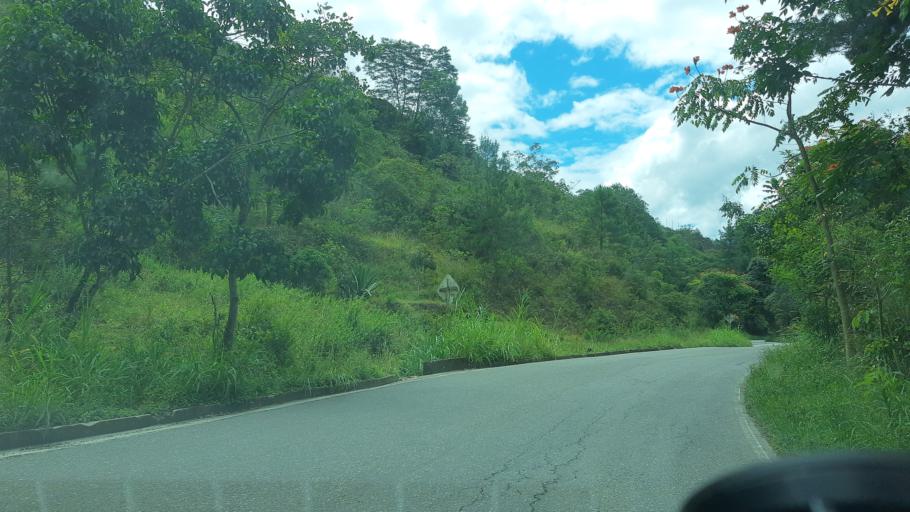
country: CO
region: Boyaca
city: Garagoa
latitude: 5.0483
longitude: -73.3872
